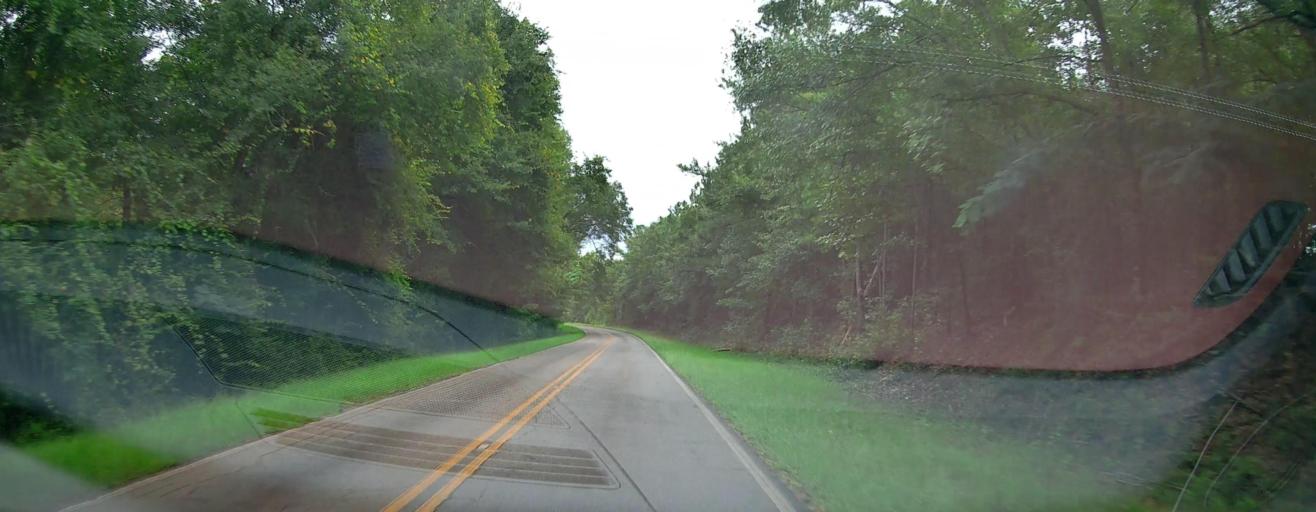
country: US
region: Georgia
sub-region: Bibb County
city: Macon
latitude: 32.7748
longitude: -83.5118
